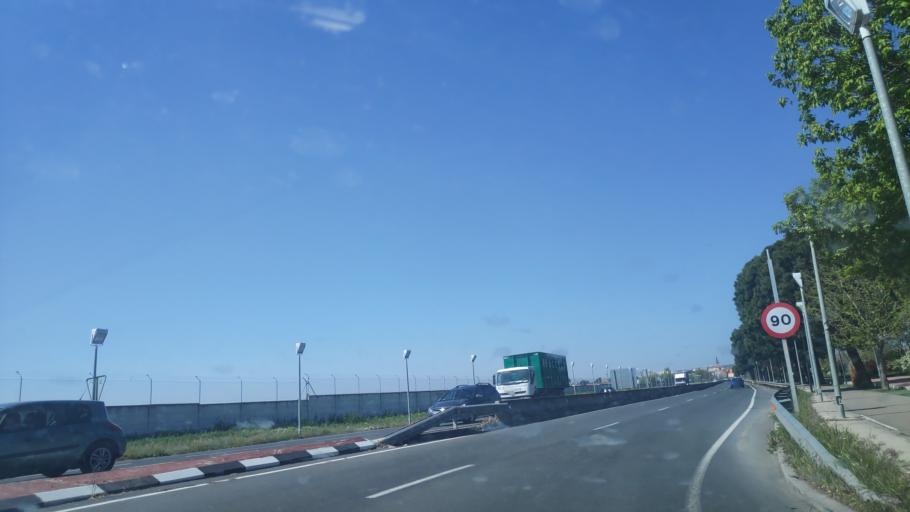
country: ES
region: Madrid
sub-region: Provincia de Madrid
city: Getafe
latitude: 40.3050
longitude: -3.7099
